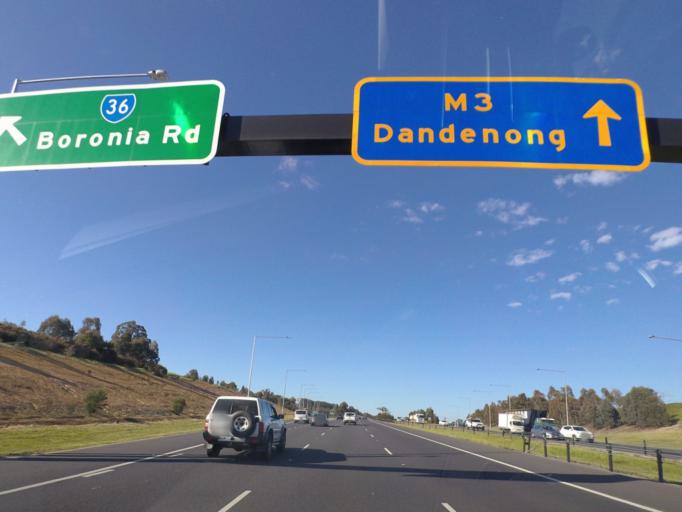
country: AU
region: Victoria
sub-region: Knox
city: Wantirna
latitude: -37.8417
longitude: 145.2179
